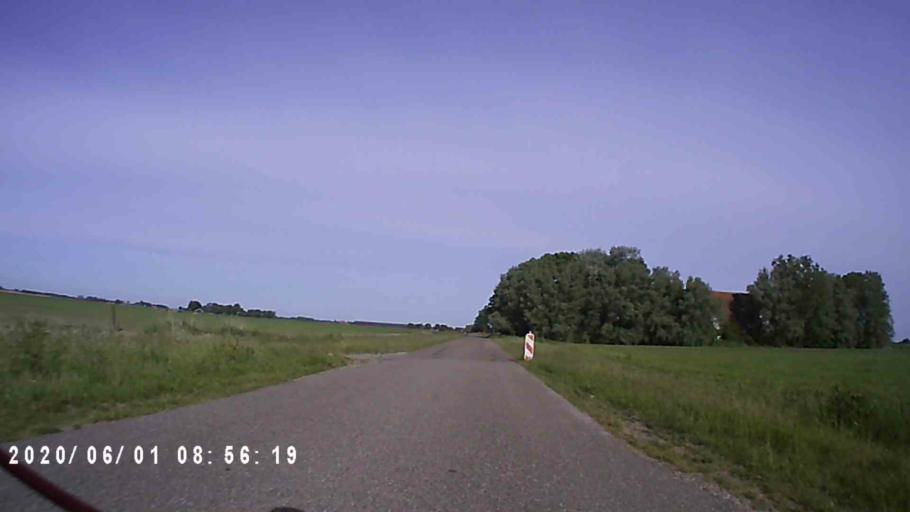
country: NL
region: Friesland
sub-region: Gemeente Leeuwarderadeel
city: Britsum
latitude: 53.2793
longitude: 5.8196
